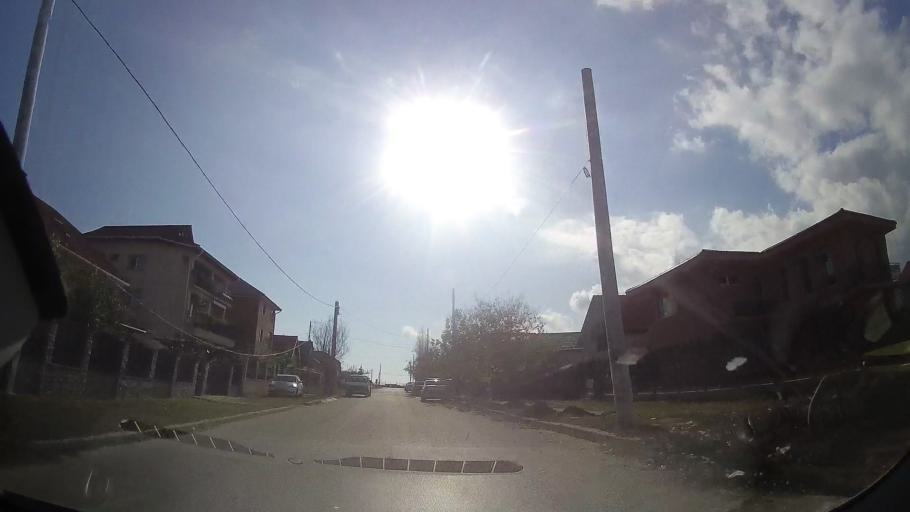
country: RO
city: Eforie Sud
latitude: 44.0158
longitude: 28.6474
